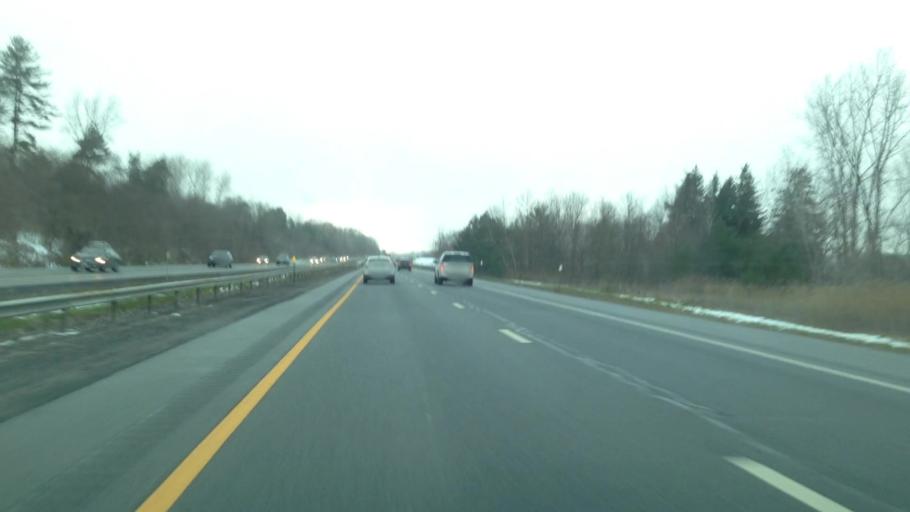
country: US
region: New York
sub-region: Montgomery County
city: Fort Plain
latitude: 42.9459
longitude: -74.6304
